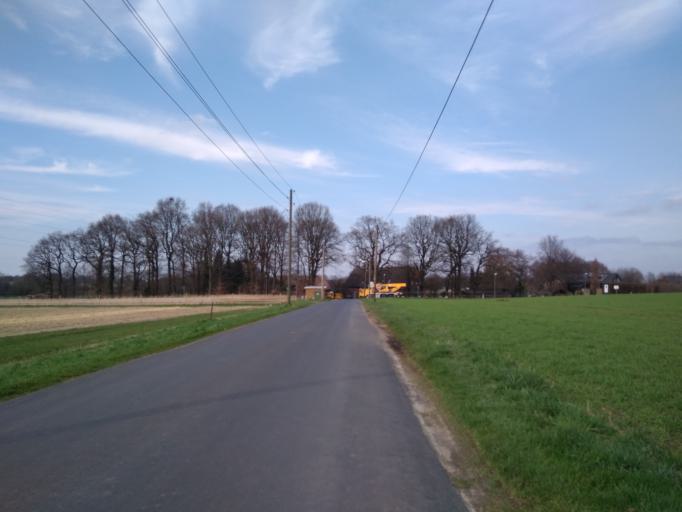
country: DE
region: North Rhine-Westphalia
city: Dorsten
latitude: 51.6197
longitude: 6.9454
